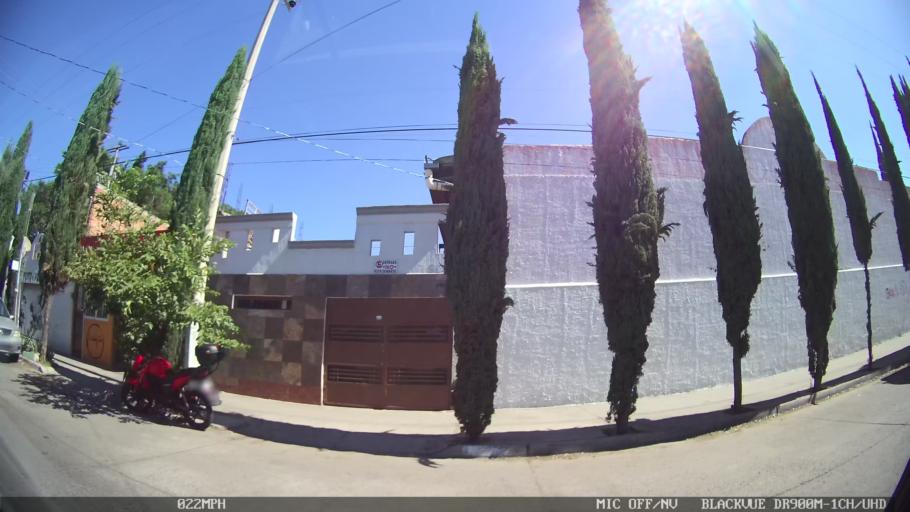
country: MX
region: Jalisco
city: Tlaquepaque
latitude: 20.6541
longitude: -103.2876
